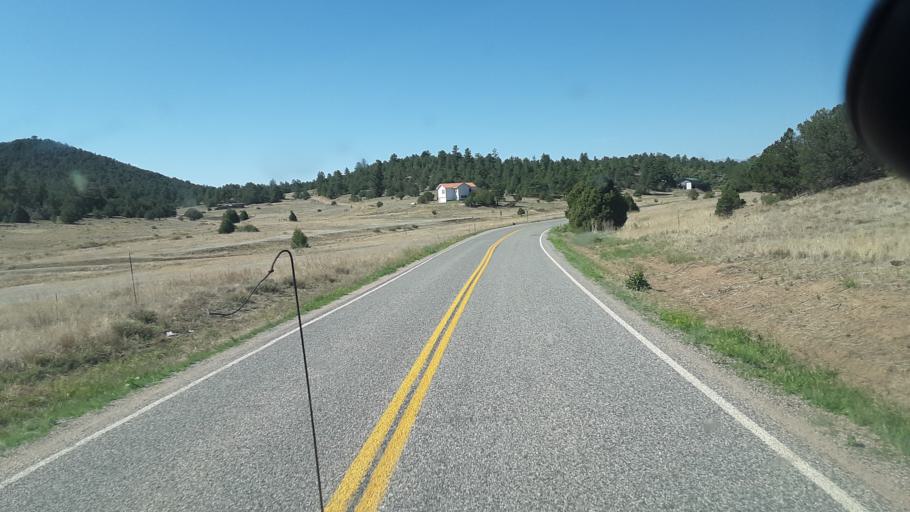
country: US
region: Colorado
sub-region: Fremont County
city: Canon City
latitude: 38.3739
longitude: -105.4565
